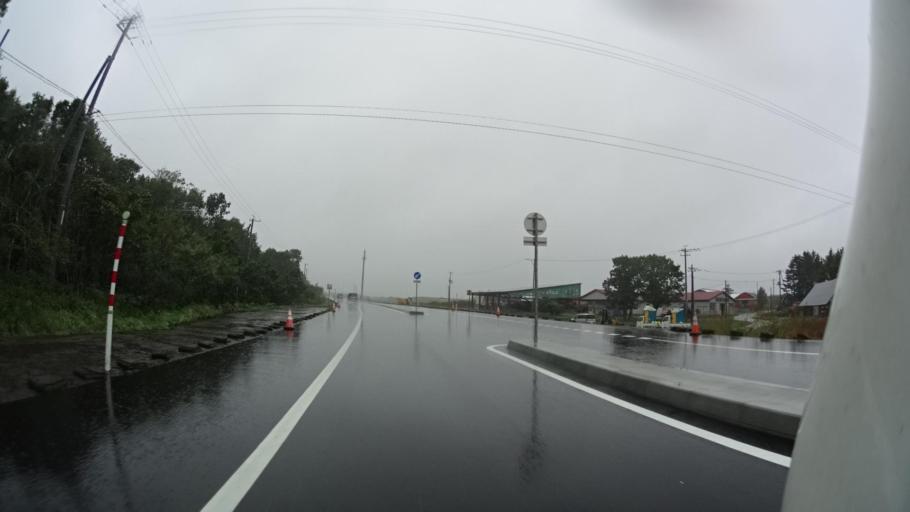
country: JP
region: Hokkaido
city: Nemuro
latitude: 43.2570
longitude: 145.3688
